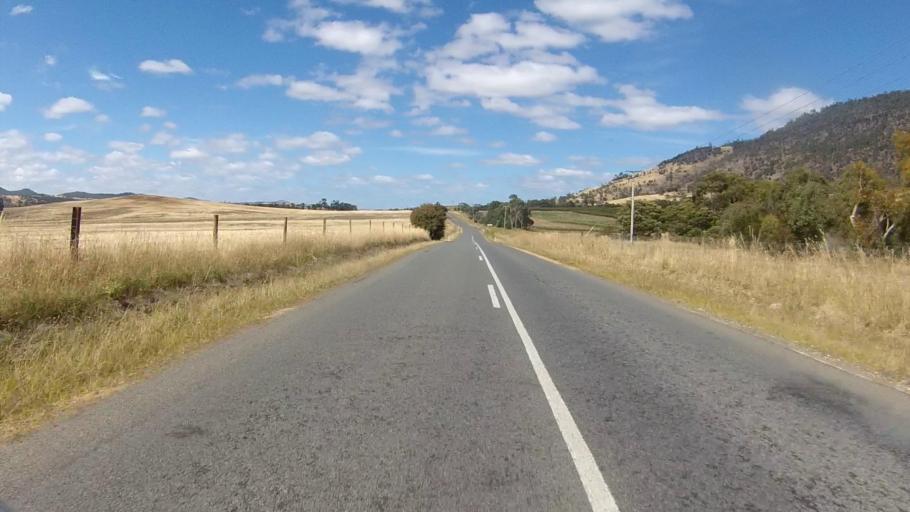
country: AU
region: Tasmania
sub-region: Sorell
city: Sorell
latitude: -42.6246
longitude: 147.4288
